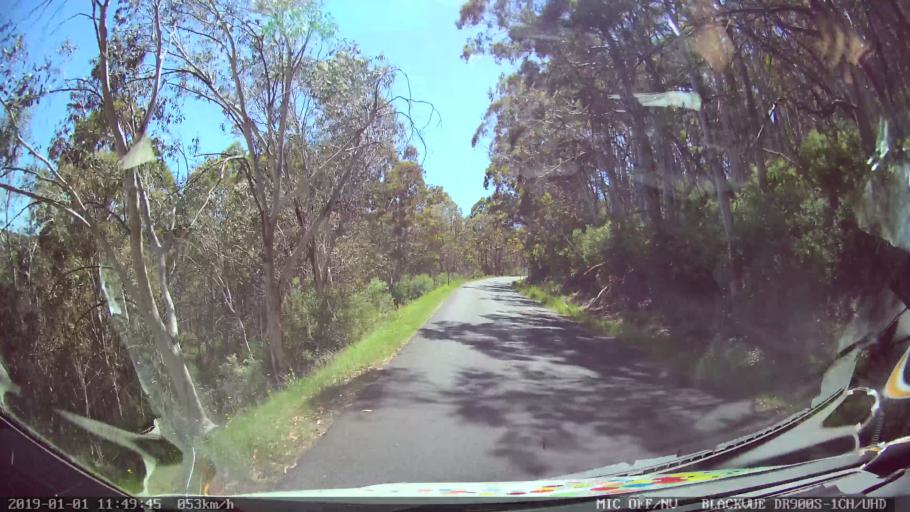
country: AU
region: New South Wales
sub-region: Snowy River
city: Jindabyne
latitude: -35.8917
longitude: 148.4147
